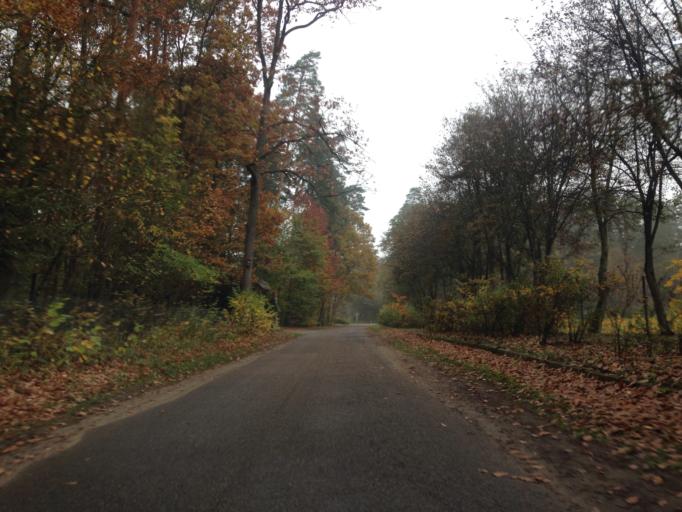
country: PL
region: Warmian-Masurian Voivodeship
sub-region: Powiat dzialdowski
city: Lidzbark
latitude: 53.2529
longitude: 19.7422
